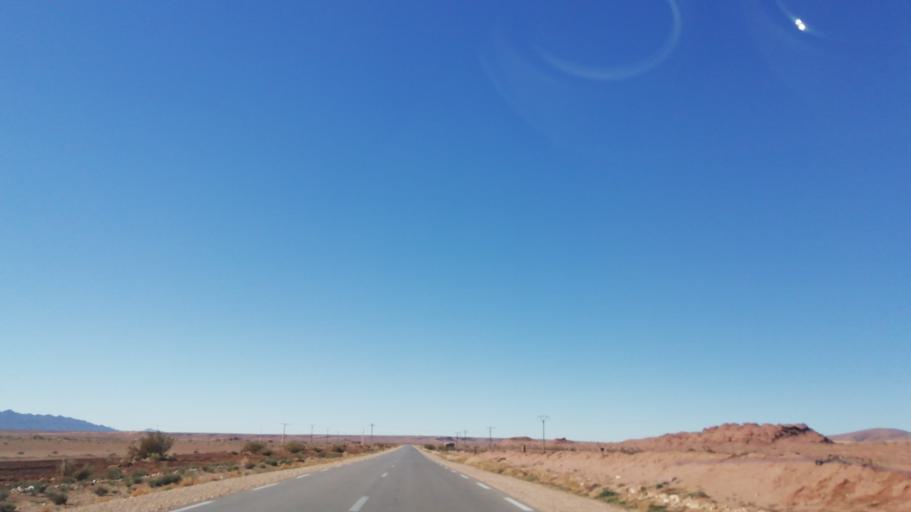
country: DZ
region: El Bayadh
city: El Abiodh Sidi Cheikh
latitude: 33.1762
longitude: 0.5308
